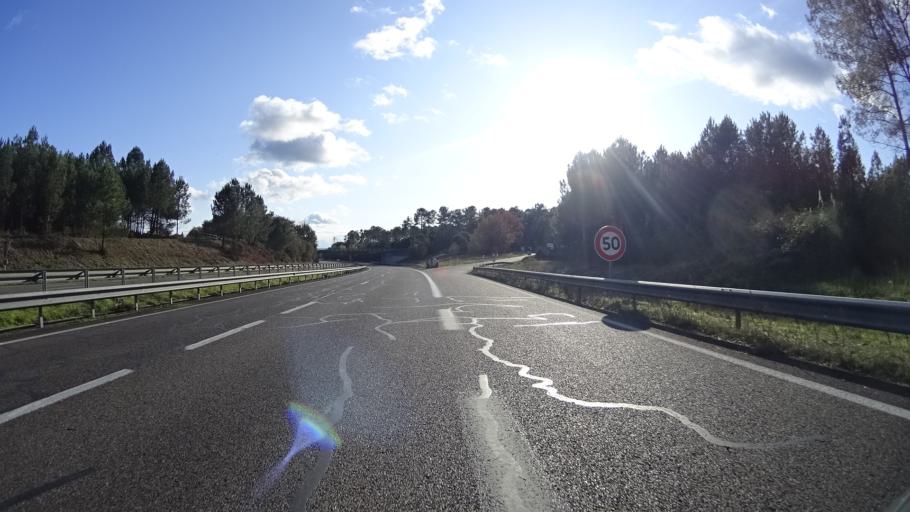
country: FR
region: Aquitaine
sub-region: Departement des Landes
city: Mees
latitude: 43.7342
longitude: -1.1021
